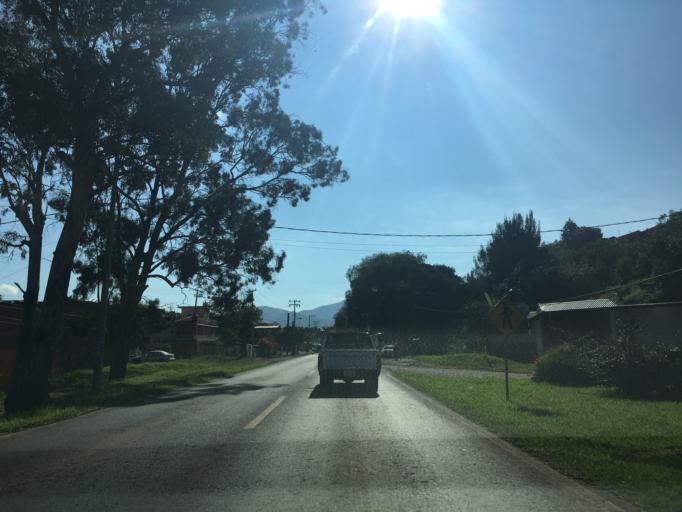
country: MX
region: Mexico
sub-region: Chalco
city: Chilchota
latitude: 19.8462
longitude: -102.1026
